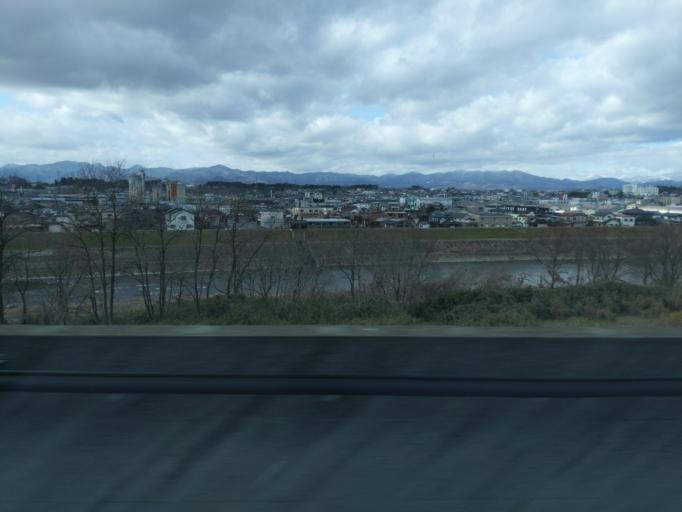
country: JP
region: Fukushima
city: Koriyama
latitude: 37.3527
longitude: 140.3724
